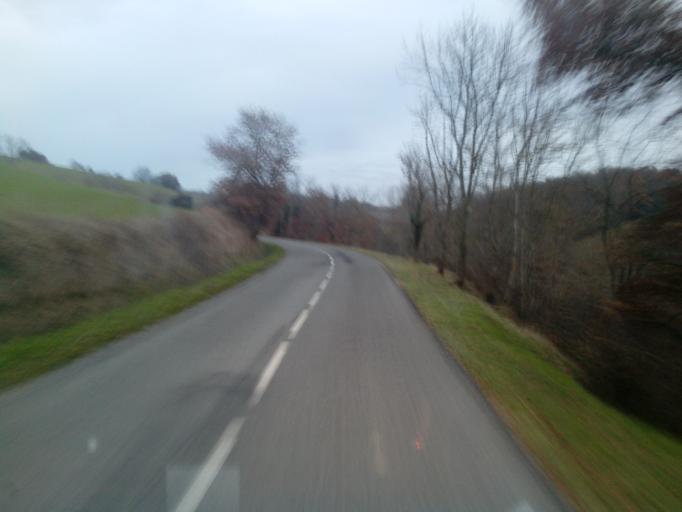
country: FR
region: Languedoc-Roussillon
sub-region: Departement de l'Aude
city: Belpech
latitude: 43.2595
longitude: 1.7421
